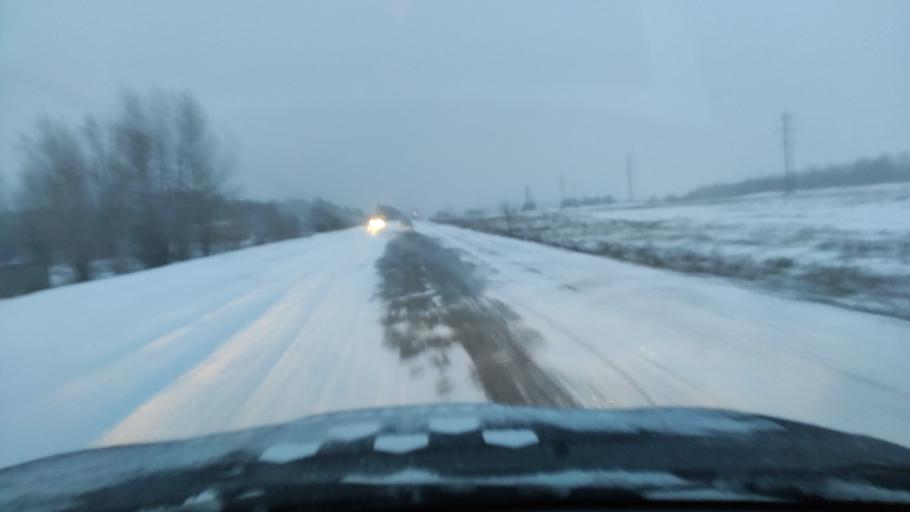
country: RU
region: Samara
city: Povolzhskiy
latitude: 53.5780
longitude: 49.6963
